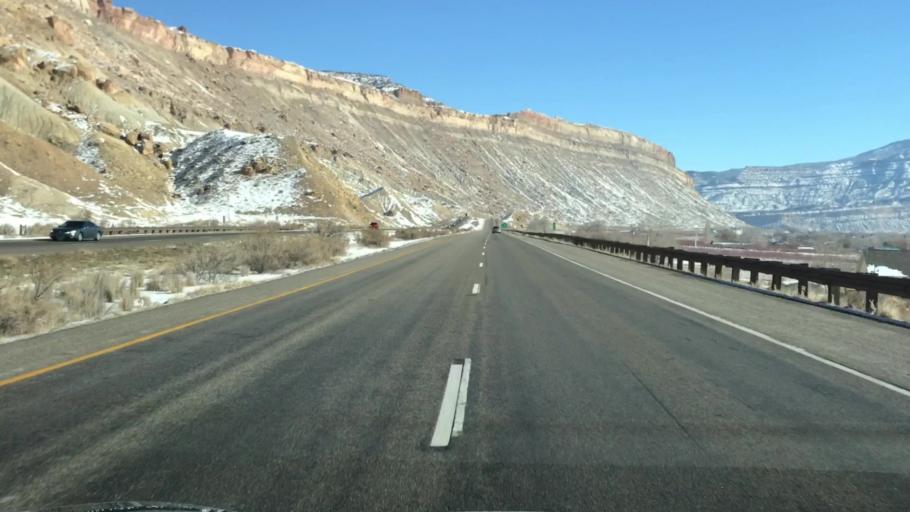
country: US
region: Colorado
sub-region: Mesa County
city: Palisade
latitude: 39.1176
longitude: -108.3889
